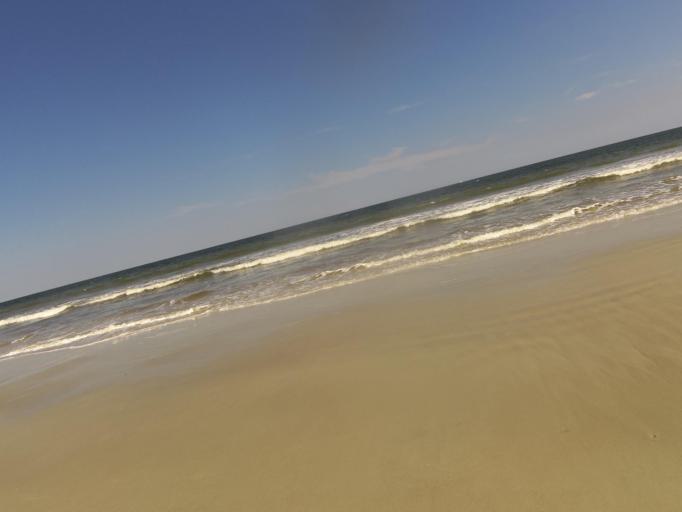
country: US
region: Florida
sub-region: Nassau County
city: Fernandina Beach
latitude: 30.6514
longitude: -81.4325
